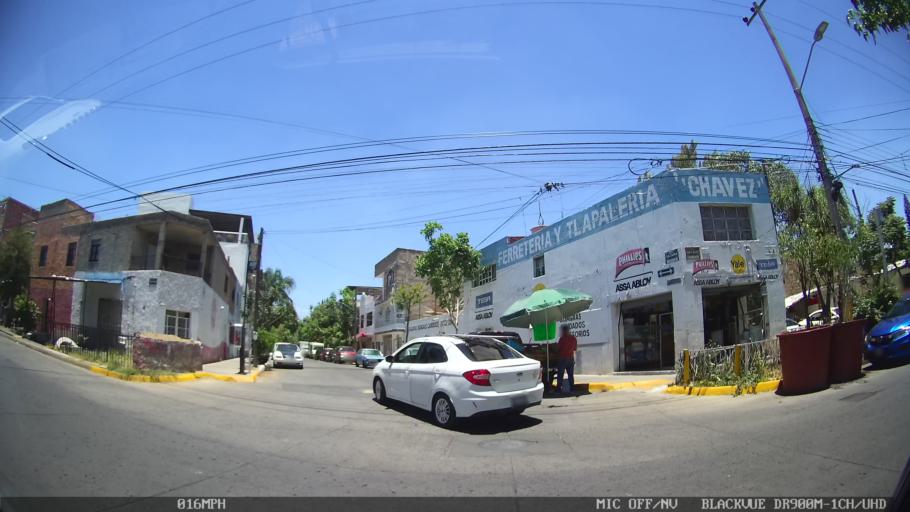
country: MX
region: Jalisco
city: Tlaquepaque
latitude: 20.6738
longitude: -103.2828
